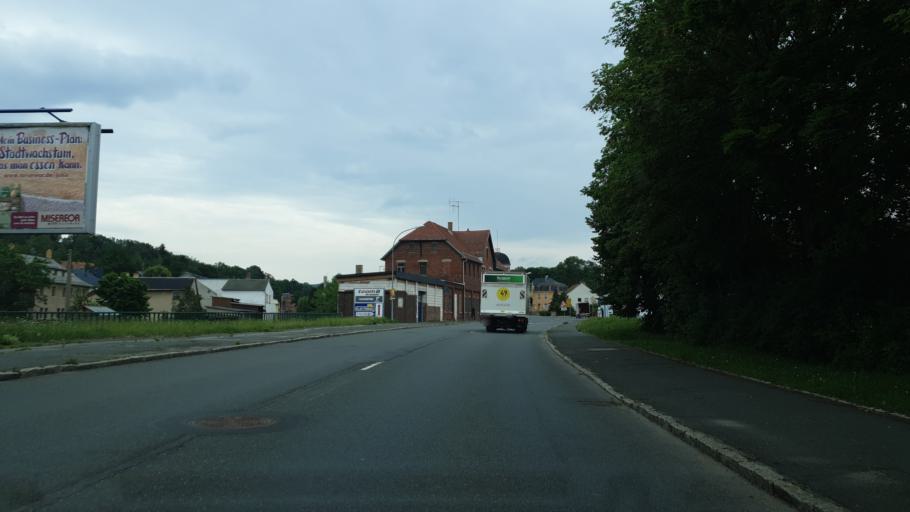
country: DE
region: Saxony
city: Rodewisch
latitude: 50.5384
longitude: 12.3995
